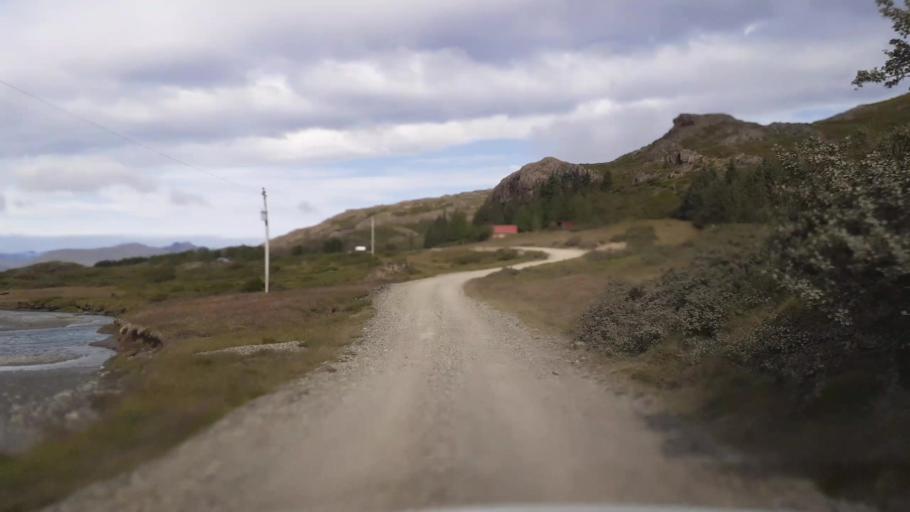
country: IS
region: East
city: Hoefn
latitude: 64.4340
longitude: -14.8952
